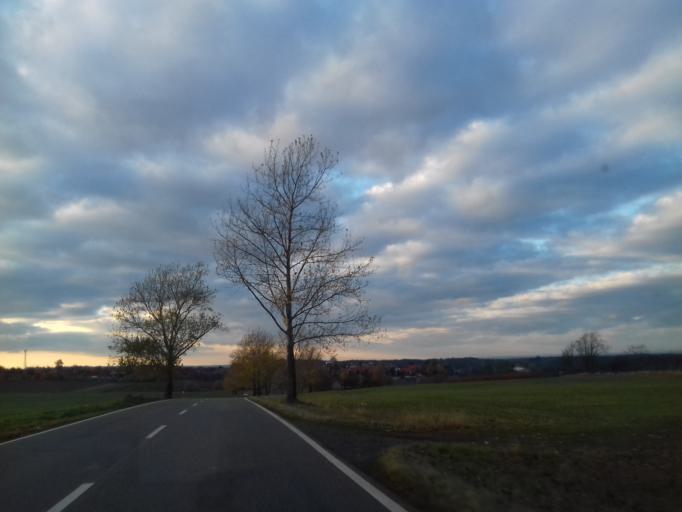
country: CZ
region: Pardubicky
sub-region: Okres Chrudim
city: Skutec
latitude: 49.8374
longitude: 16.0140
